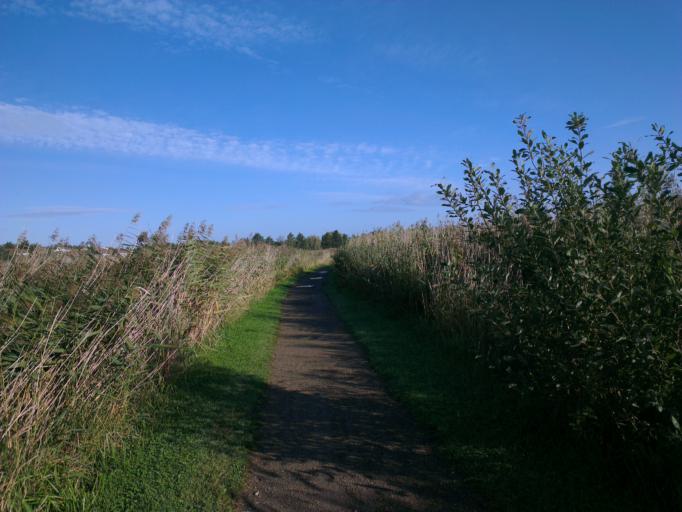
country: DK
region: Capital Region
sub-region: Frederikssund Kommune
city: Frederikssund
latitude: 55.8537
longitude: 12.0808
